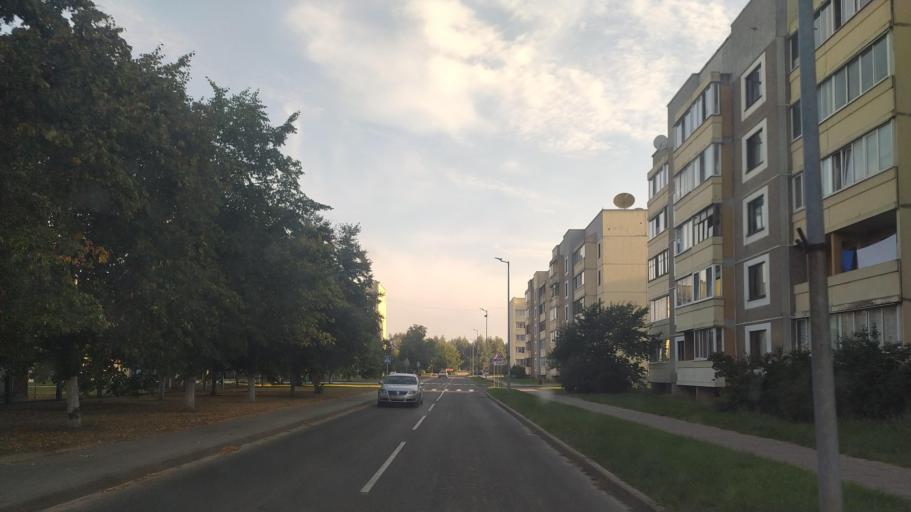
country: BY
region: Brest
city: Byaroza
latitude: 52.5465
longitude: 24.9843
